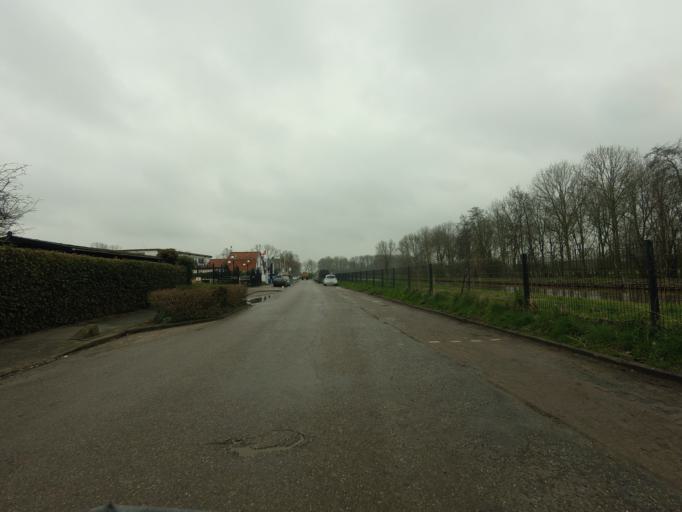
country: NL
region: Utrecht
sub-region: Stichtse Vecht
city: Breukelen
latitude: 52.1773
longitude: 5.0209
